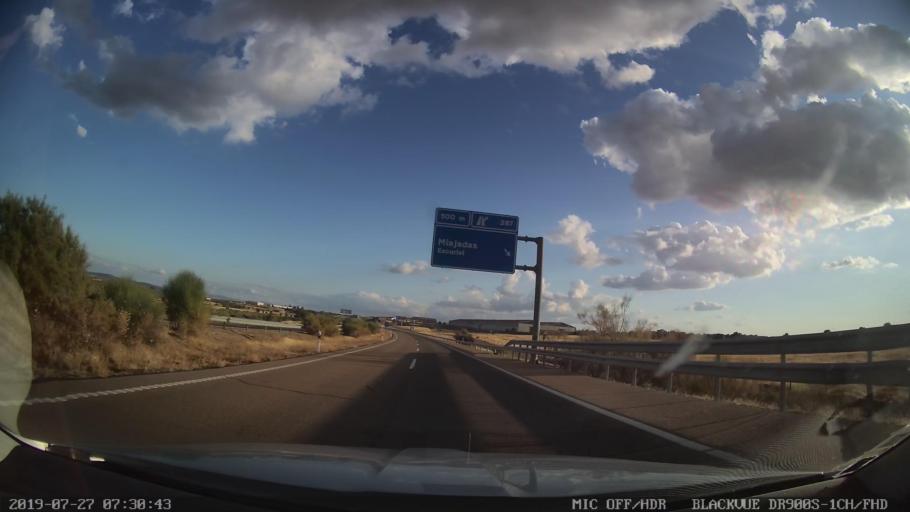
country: ES
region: Extremadura
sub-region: Provincia de Caceres
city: Escurial
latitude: 39.1842
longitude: -5.8960
